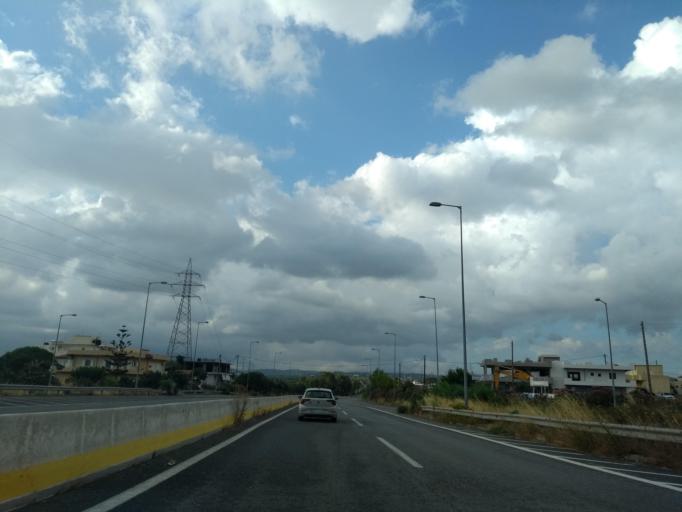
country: GR
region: Crete
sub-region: Nomos Irakleiou
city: Gazi
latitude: 35.3380
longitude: 25.0505
